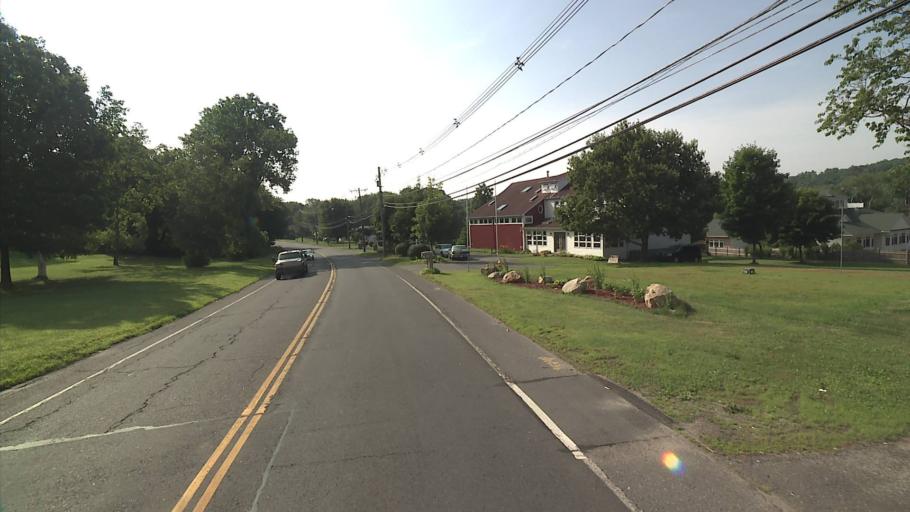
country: US
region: Connecticut
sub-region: New Haven County
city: Prospect
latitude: 41.5445
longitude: -72.9783
